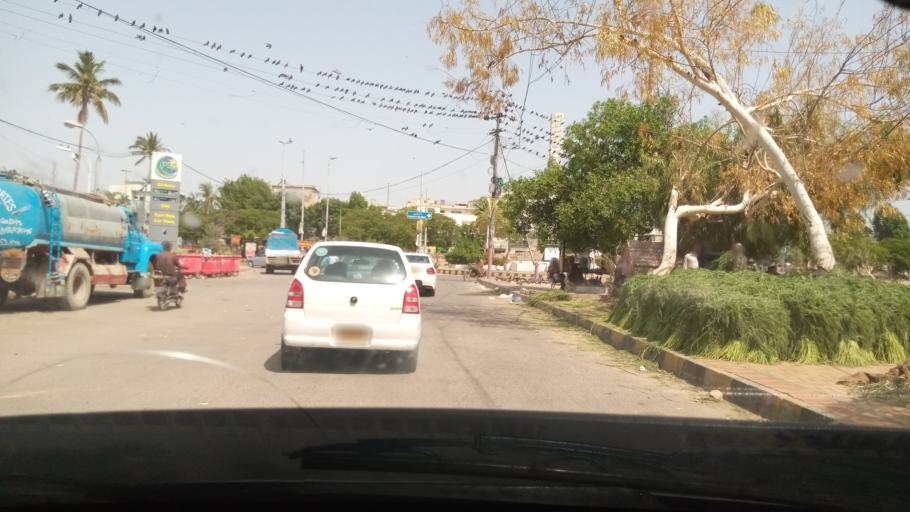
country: PK
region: Sindh
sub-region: Karachi District
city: Karachi
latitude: 24.8732
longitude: 67.0481
